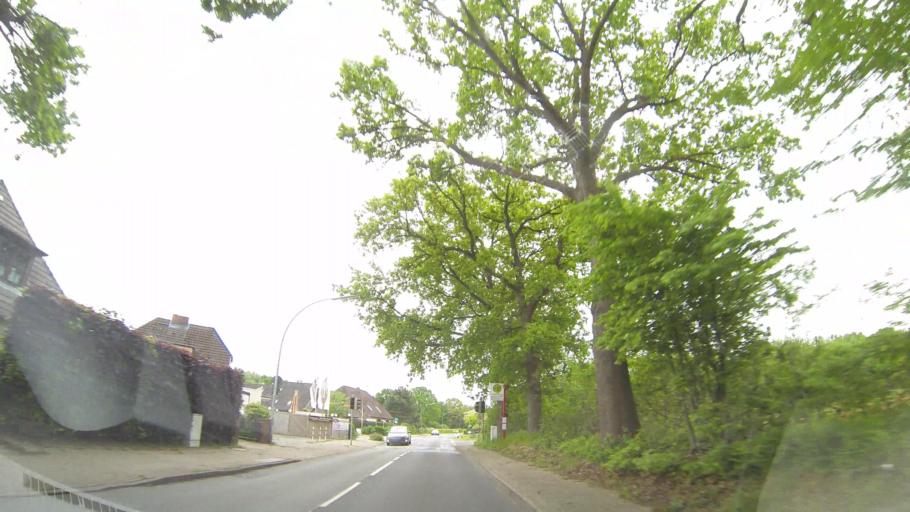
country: DE
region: Schleswig-Holstein
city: Ellerbek
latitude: 53.6418
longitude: 9.8707
